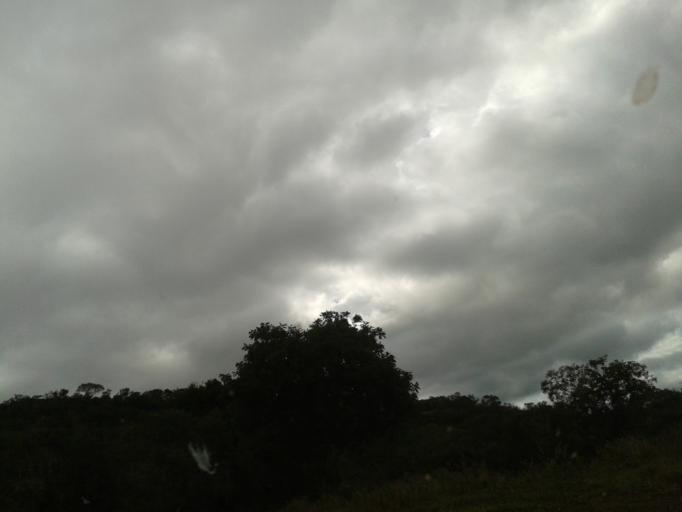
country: BR
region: Minas Gerais
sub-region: Campina Verde
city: Campina Verde
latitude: -19.4610
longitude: -49.5889
